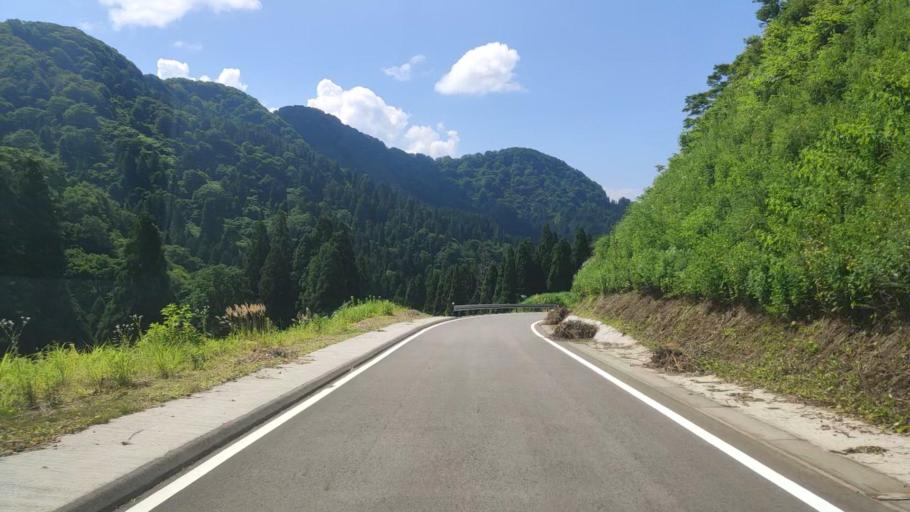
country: JP
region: Fukui
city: Katsuyama
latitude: 36.1449
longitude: 136.5202
